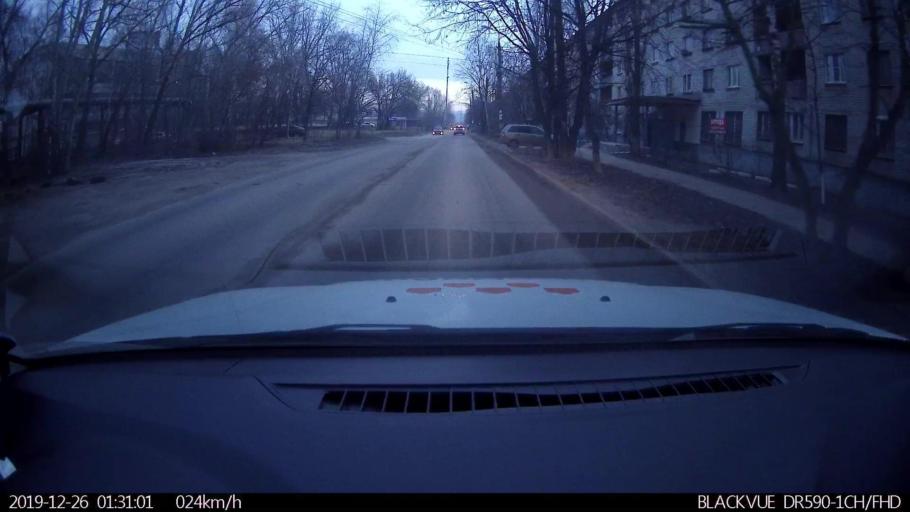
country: RU
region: Nizjnij Novgorod
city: Nizhniy Novgorod
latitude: 56.2699
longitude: 43.8962
